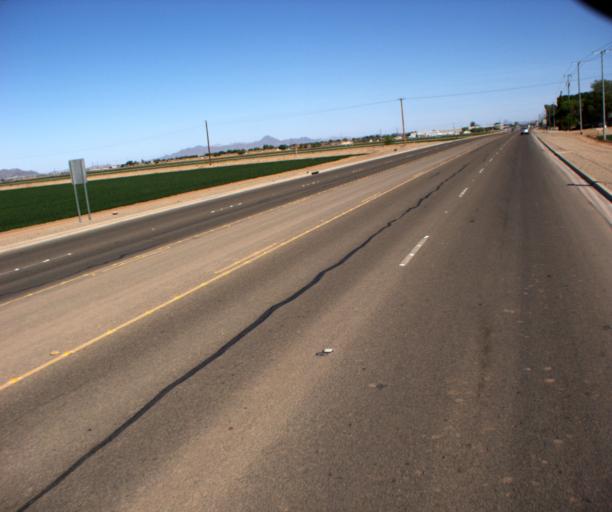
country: US
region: Arizona
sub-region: Yuma County
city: Yuma
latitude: 32.6607
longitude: -114.6500
